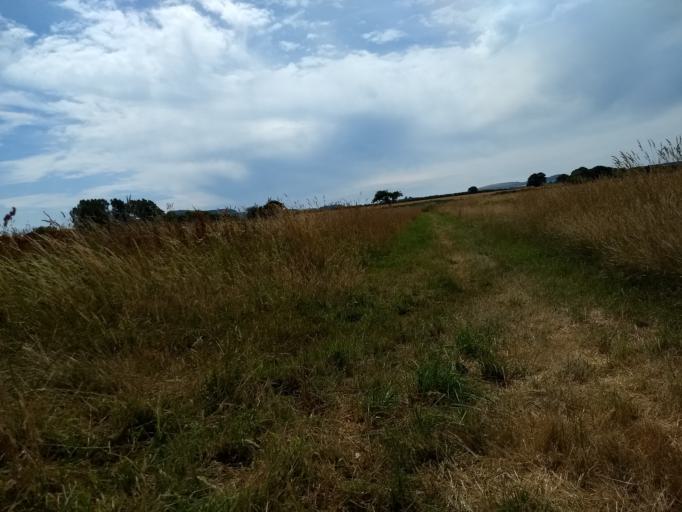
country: GB
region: England
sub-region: Isle of Wight
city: Newchurch
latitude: 50.6523
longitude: -1.2433
